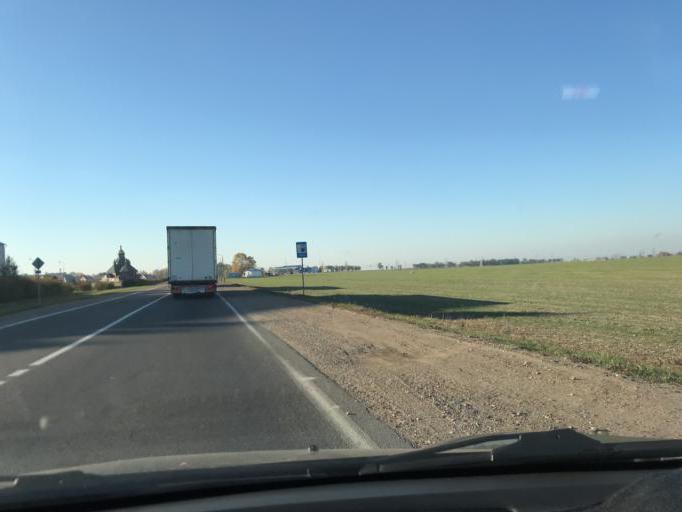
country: BY
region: Minsk
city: Slutsk
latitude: 53.0471
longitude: 27.5683
